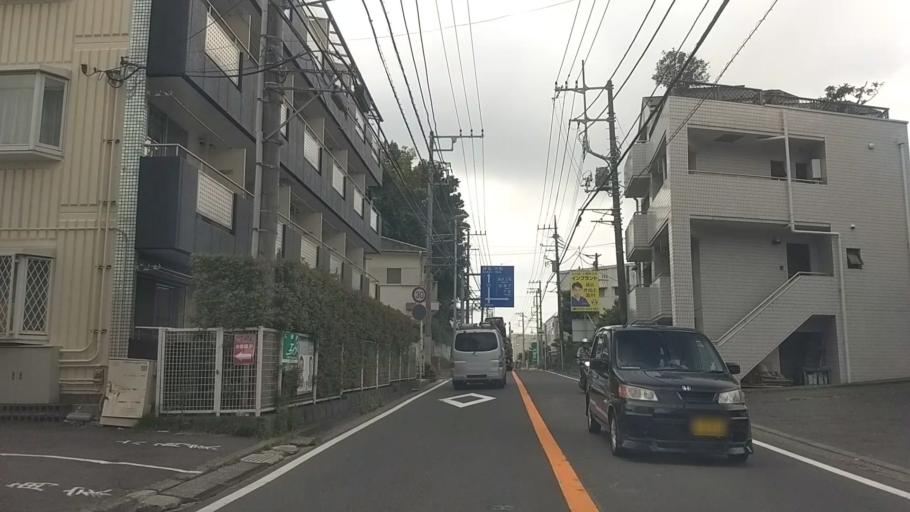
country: JP
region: Kanagawa
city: Kamakura
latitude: 35.3834
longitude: 139.5364
